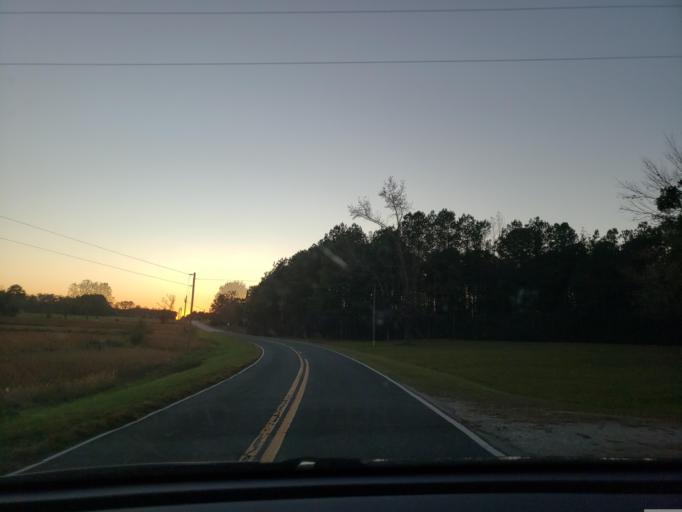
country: US
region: North Carolina
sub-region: Duplin County
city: Beulaville
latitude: 34.7607
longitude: -77.6773
